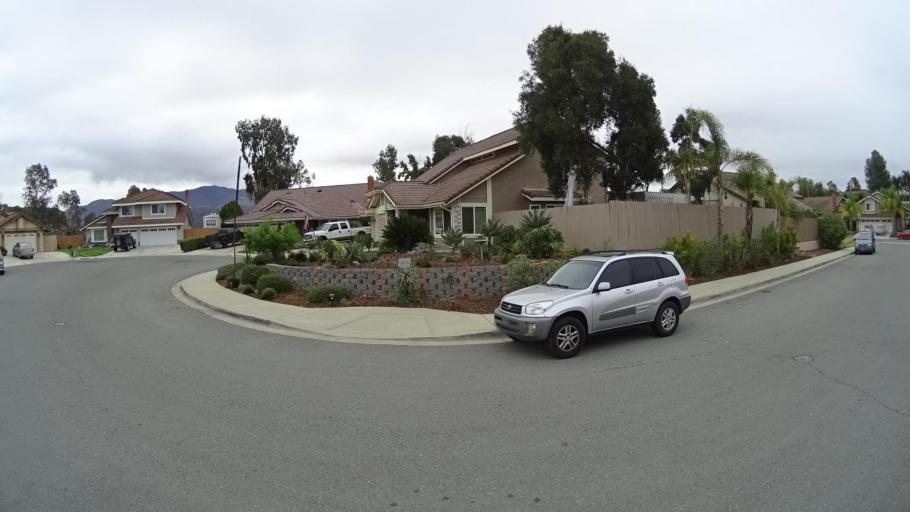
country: US
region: California
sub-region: San Diego County
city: Rancho San Diego
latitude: 32.7603
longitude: -116.9086
